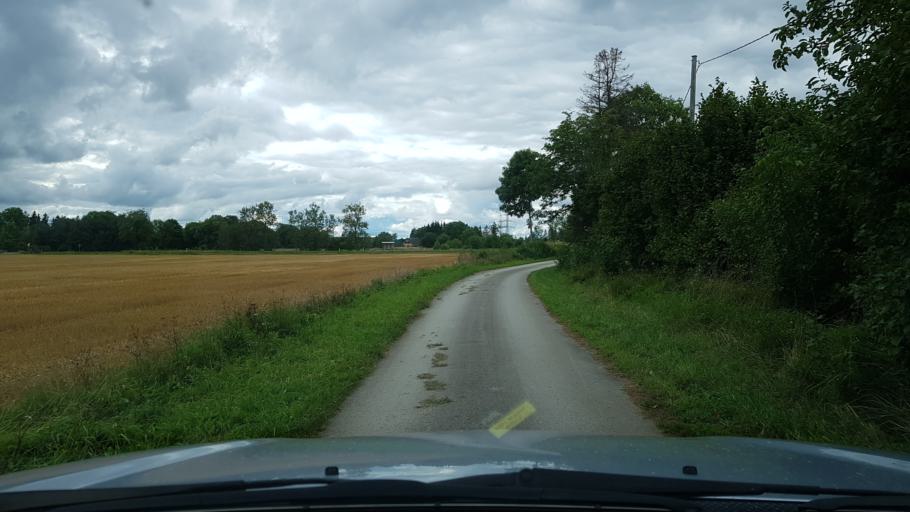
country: EE
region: Harju
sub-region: Rae vald
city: Vaida
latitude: 59.2750
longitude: 25.0111
